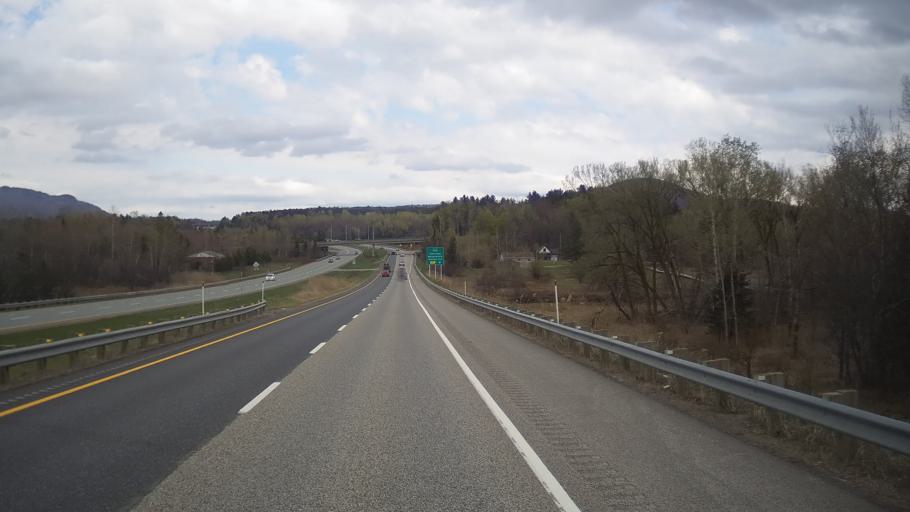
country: CA
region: Quebec
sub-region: Estrie
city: Magog
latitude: 45.2994
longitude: -72.3235
